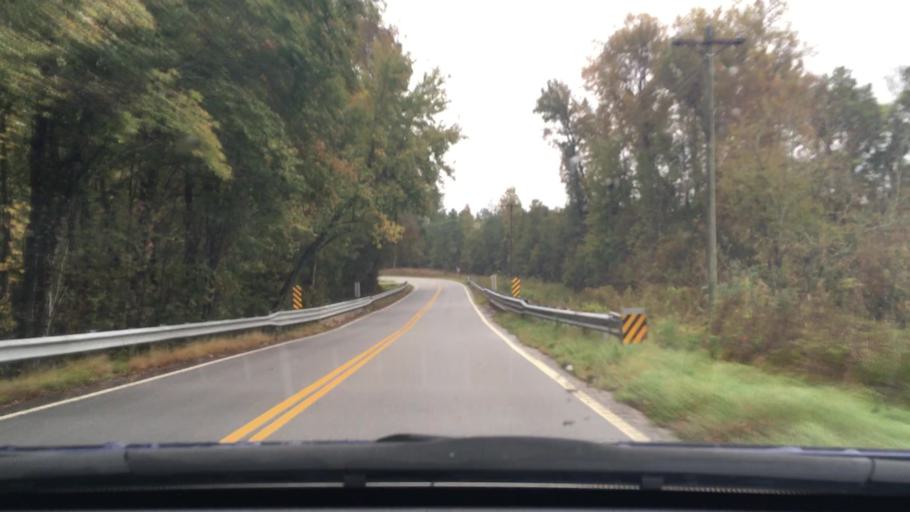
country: US
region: South Carolina
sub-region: Darlington County
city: Darlington
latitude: 34.2935
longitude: -79.9222
